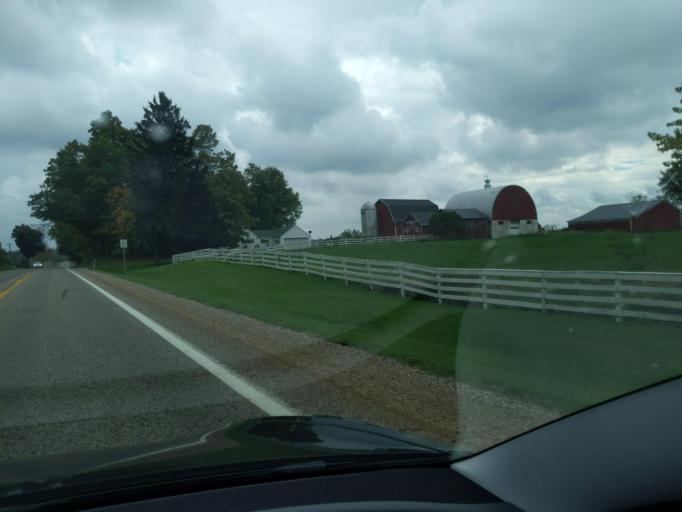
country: US
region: Michigan
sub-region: Eaton County
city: Potterville
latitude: 42.5460
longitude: -84.7449
